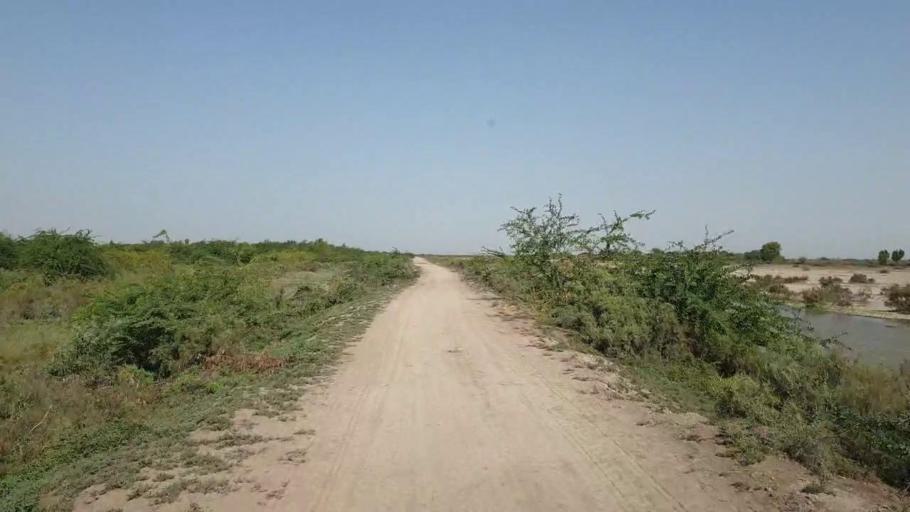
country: PK
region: Sindh
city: Tando Bago
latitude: 24.6466
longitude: 69.0718
